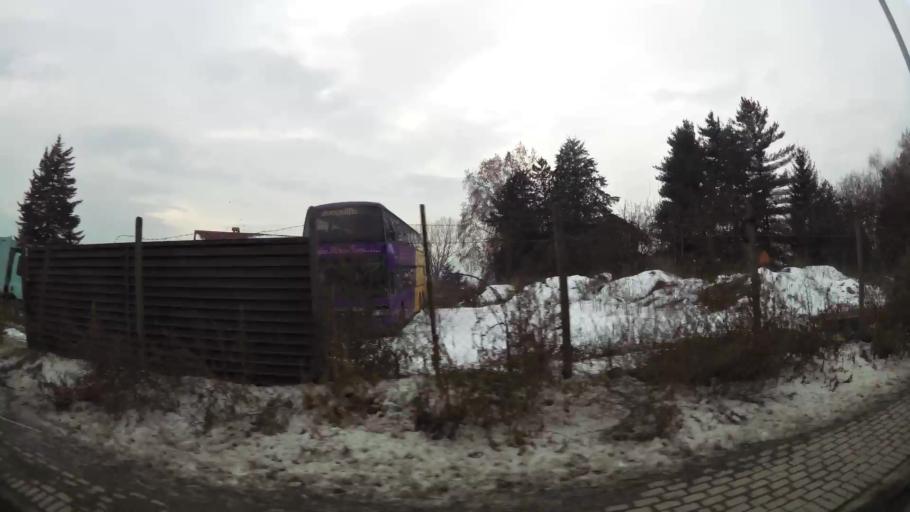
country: MK
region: Butel
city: Butel
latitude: 42.0360
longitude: 21.4443
